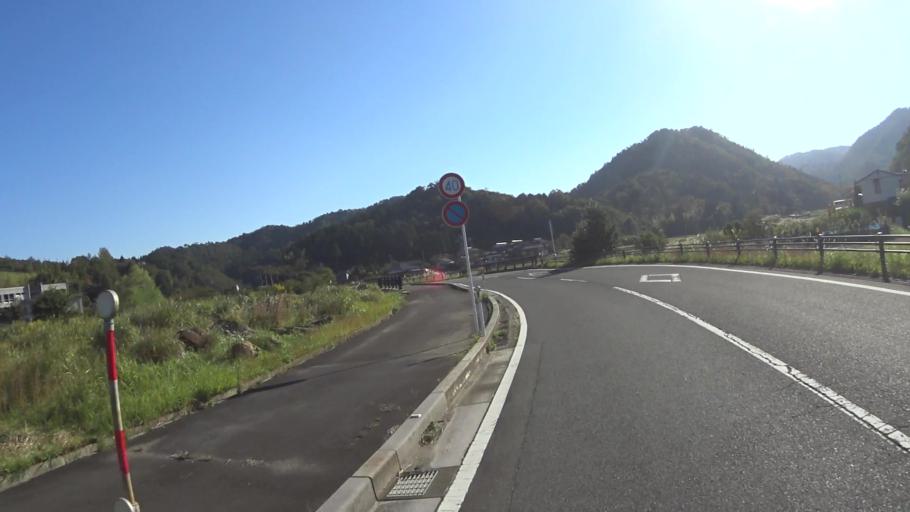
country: JP
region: Hyogo
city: Toyooka
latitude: 35.6288
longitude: 134.8877
